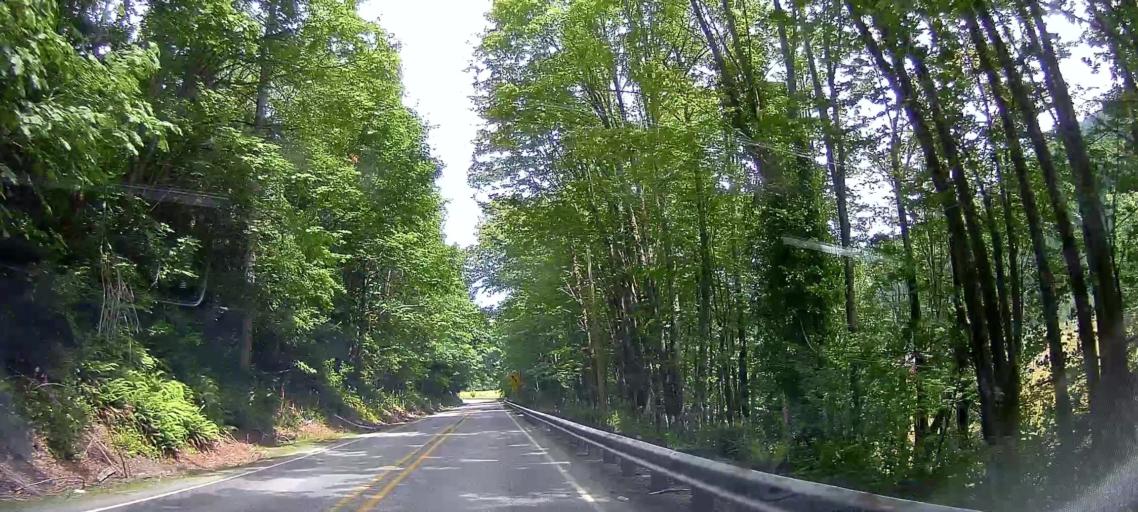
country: US
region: Washington
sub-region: Skagit County
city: Sedro-Woolley
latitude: 48.6325
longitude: -122.2158
